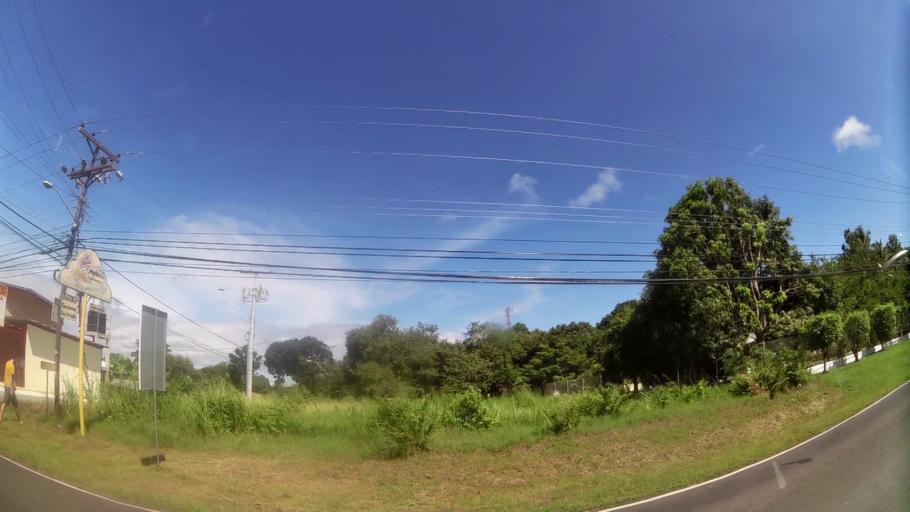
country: PA
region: Panama
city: Chame
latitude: 8.5633
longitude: -79.8899
